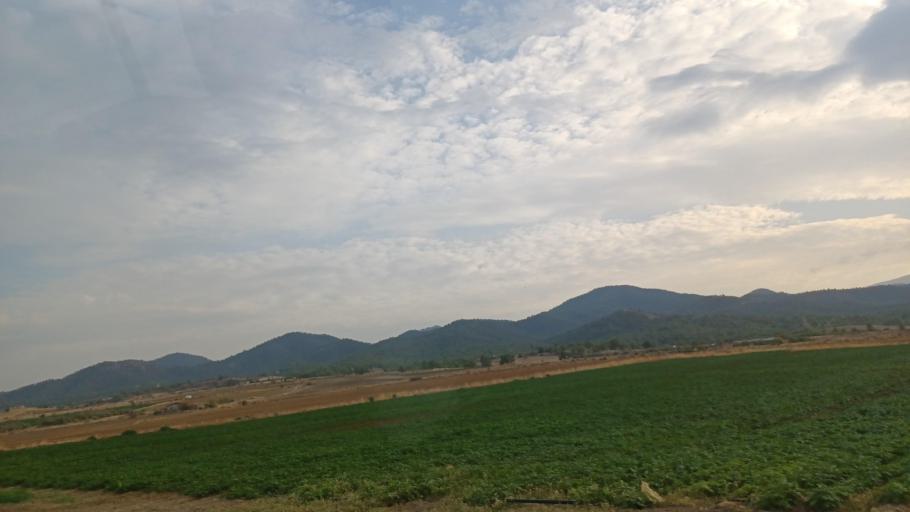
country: CY
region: Lefkosia
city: Astromeritis
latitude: 35.0833
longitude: 32.9616
